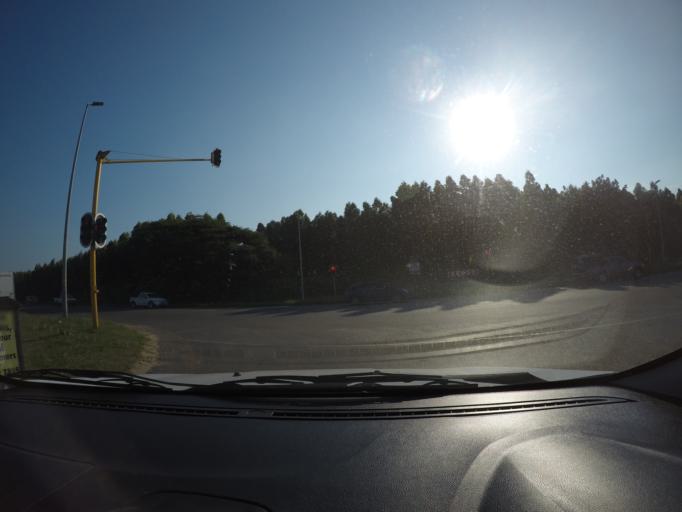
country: ZA
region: KwaZulu-Natal
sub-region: uThungulu District Municipality
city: Richards Bay
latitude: -28.7153
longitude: 32.0308
